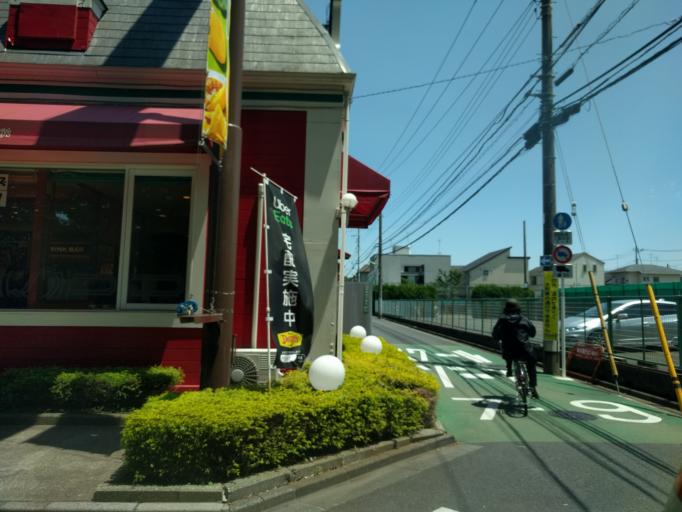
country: JP
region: Tokyo
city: Chofugaoka
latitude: 35.6504
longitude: 139.5967
